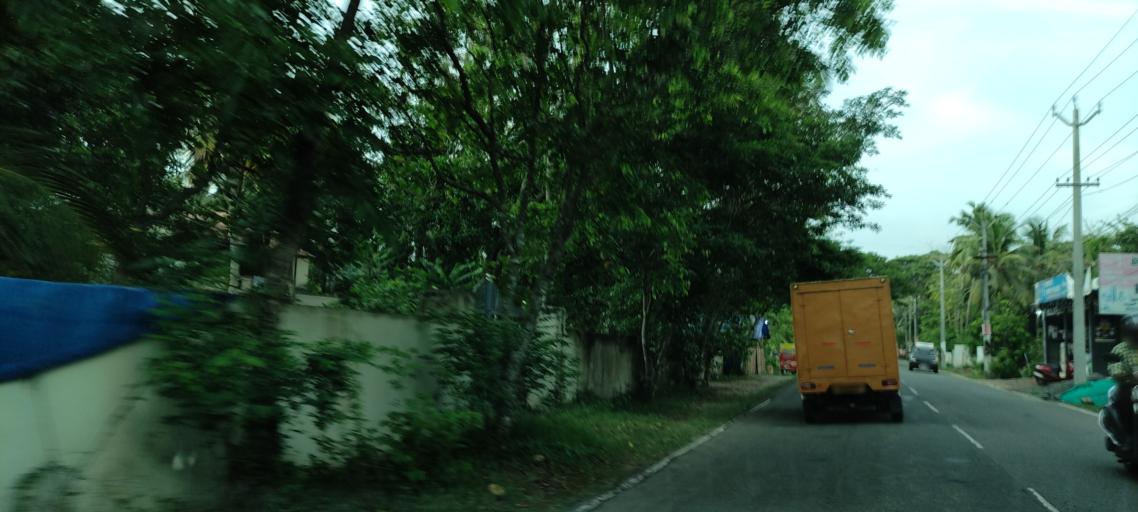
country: IN
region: Kerala
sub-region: Kottayam
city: Vaikam
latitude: 9.7596
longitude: 76.3626
